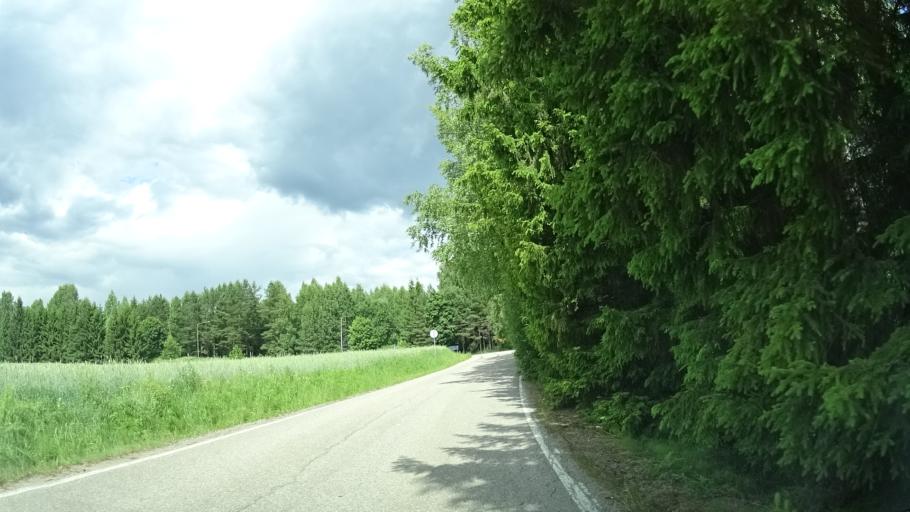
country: FI
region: Uusimaa
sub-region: Helsinki
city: Vihti
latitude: 60.4291
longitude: 24.5287
